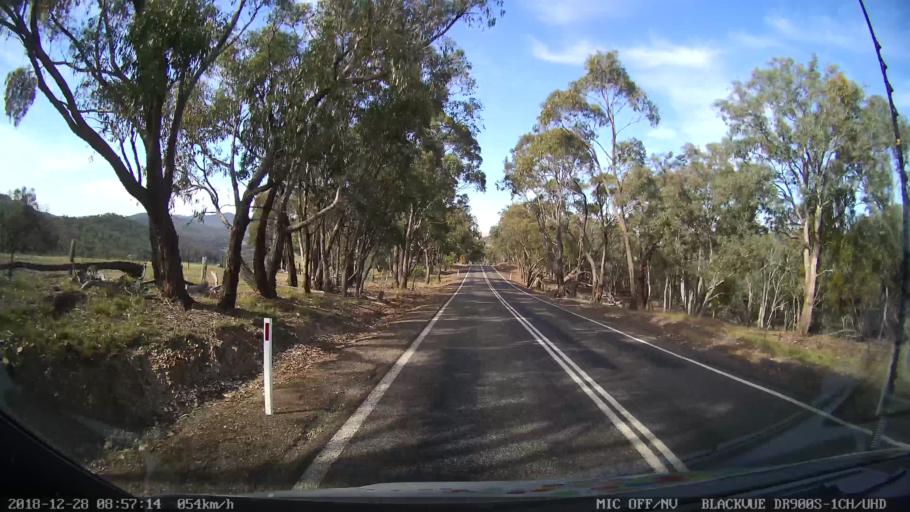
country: AU
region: New South Wales
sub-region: Upper Lachlan Shire
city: Crookwell
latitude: -34.1173
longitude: 149.3367
